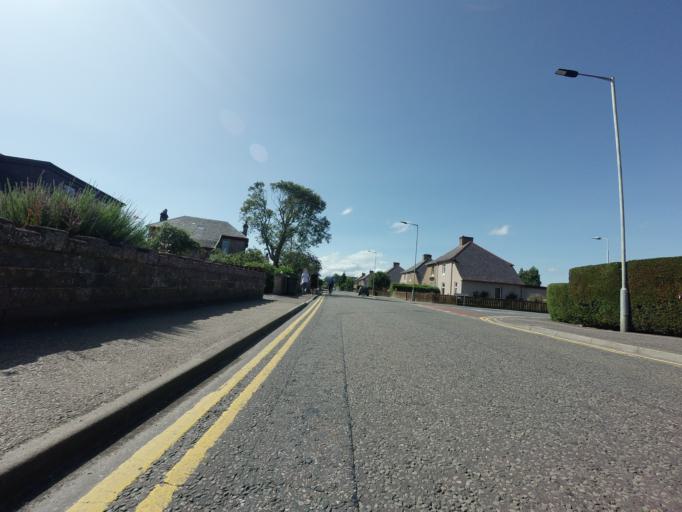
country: GB
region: Scotland
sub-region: Highland
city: Inverness
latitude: 57.4744
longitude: -4.2114
